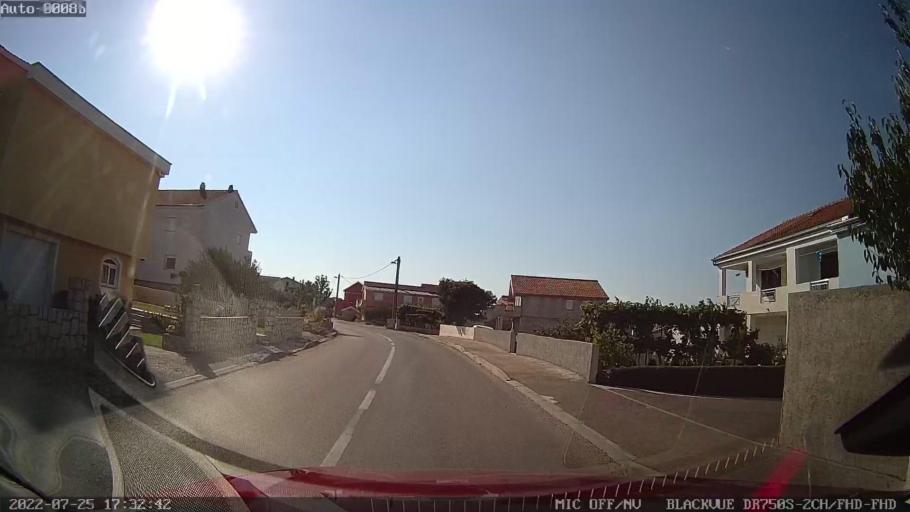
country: HR
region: Zadarska
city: Posedarje
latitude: 44.1780
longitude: 15.4907
